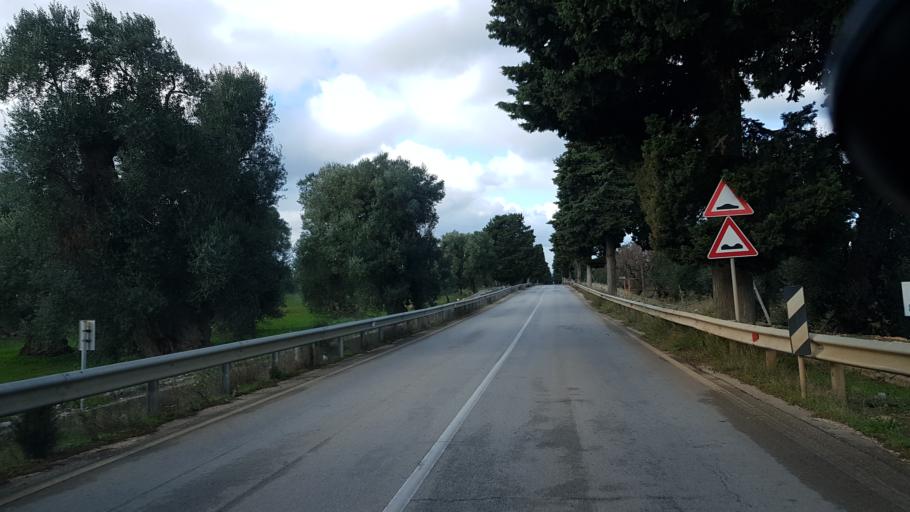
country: IT
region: Apulia
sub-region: Provincia di Brindisi
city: Montalbano
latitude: 40.7599
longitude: 17.5302
